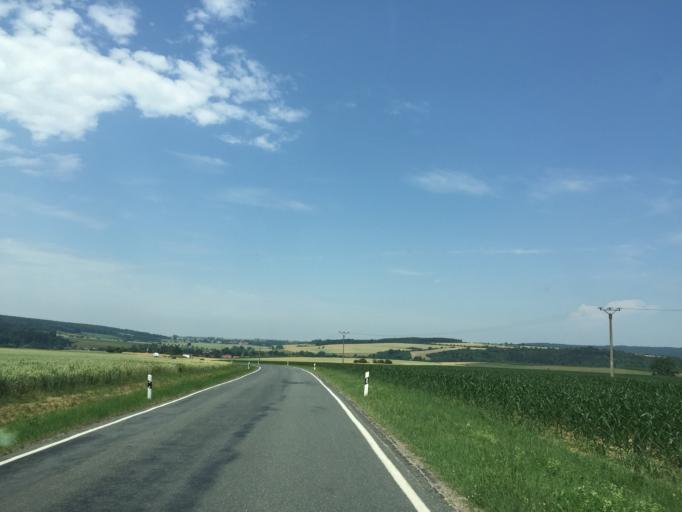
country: DE
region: Thuringia
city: Barchfeld
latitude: 50.7967
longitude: 11.1841
